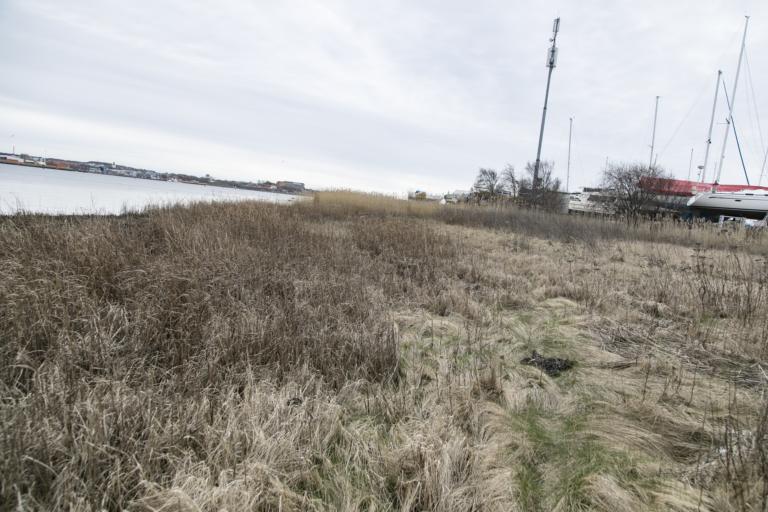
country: SE
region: Halland
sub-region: Varbergs Kommun
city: Varberg
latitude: 57.1183
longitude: 12.2272
